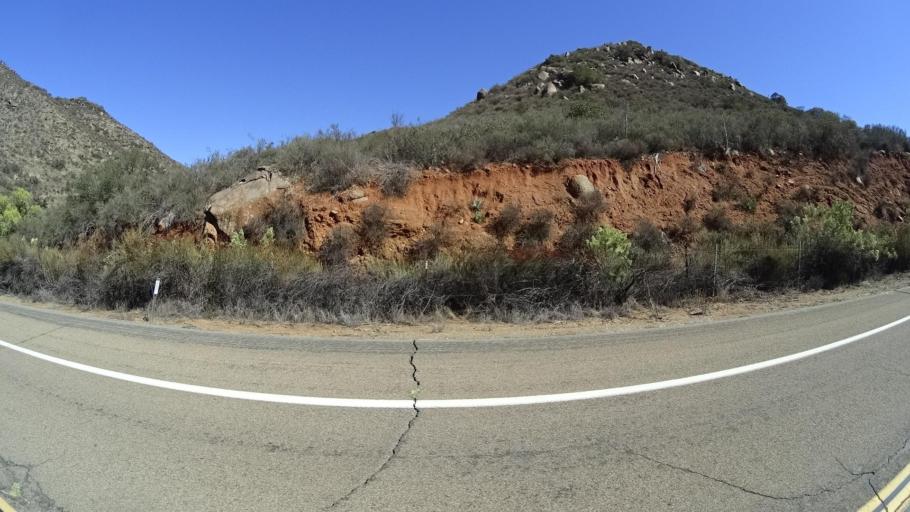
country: US
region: California
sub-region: San Diego County
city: Alpine
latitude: 32.7993
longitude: -116.7484
